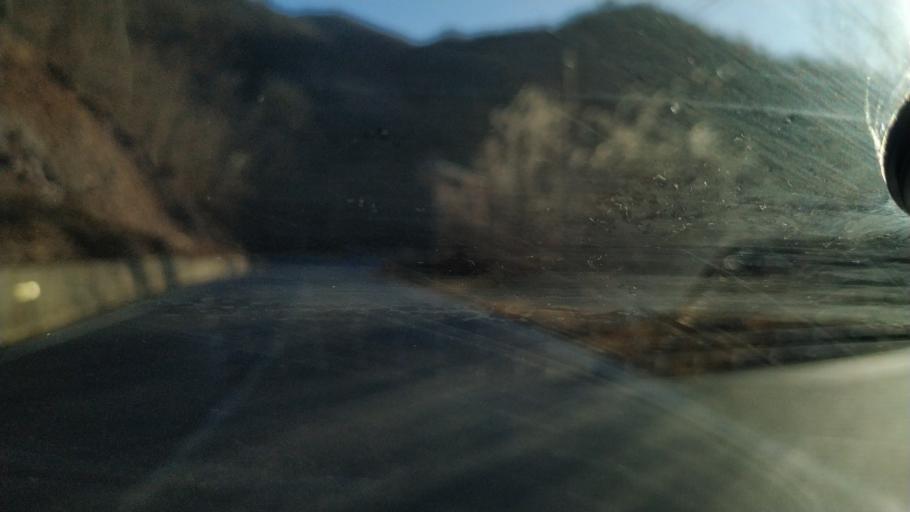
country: IT
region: Piedmont
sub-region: Provincia di Biella
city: Sostegno
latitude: 45.6687
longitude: 8.2589
